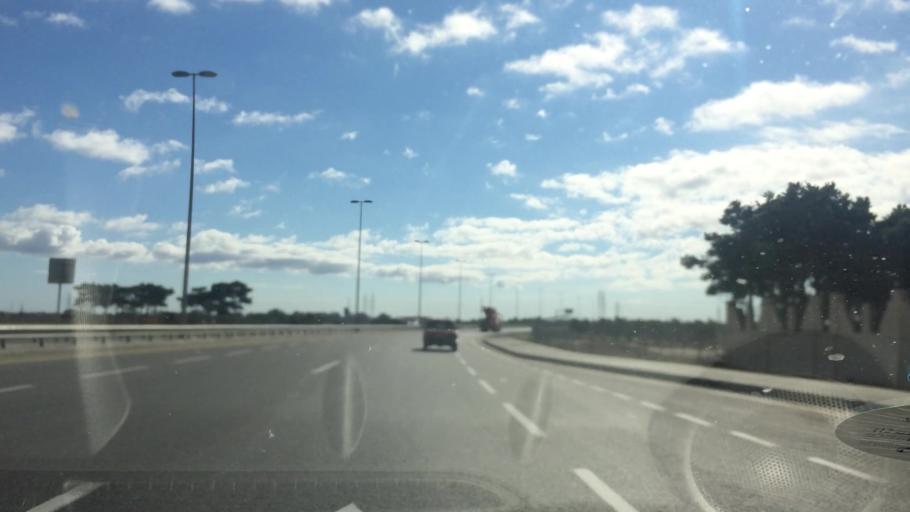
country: AZ
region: Baki
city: Qala
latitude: 40.4424
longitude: 50.1797
